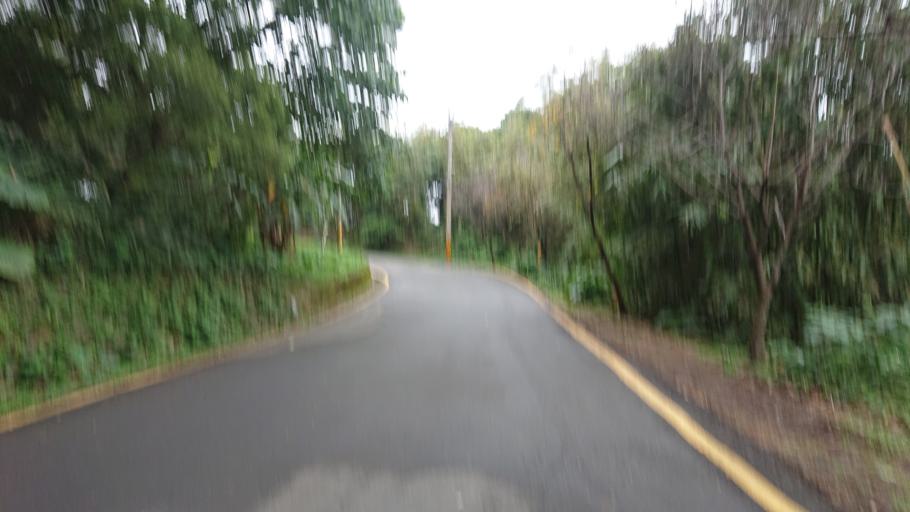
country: TW
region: Taiwan
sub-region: Taoyuan
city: Taoyuan
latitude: 24.9324
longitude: 121.3665
